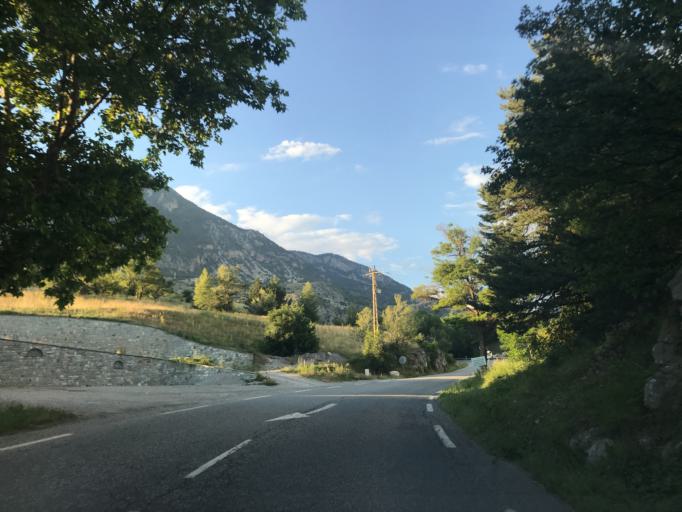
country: FR
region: Provence-Alpes-Cote d'Azur
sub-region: Departement des Hautes-Alpes
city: Guillestre
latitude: 44.6631
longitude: 6.6615
